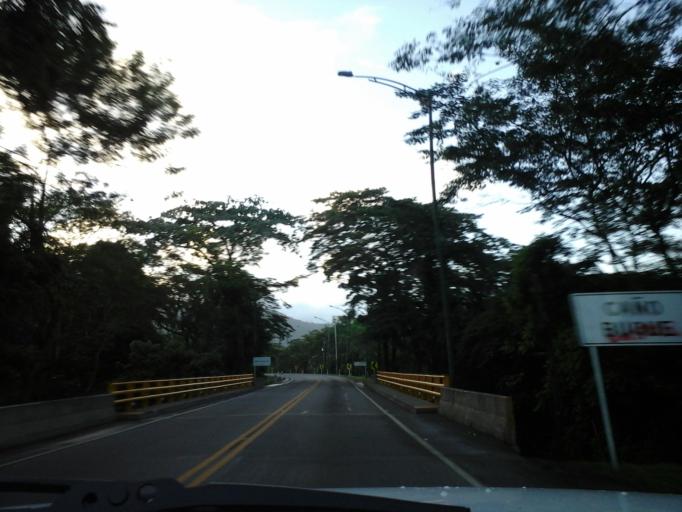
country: CO
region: Meta
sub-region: Villavicencio
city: Villavicencio
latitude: 4.1374
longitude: -73.6561
